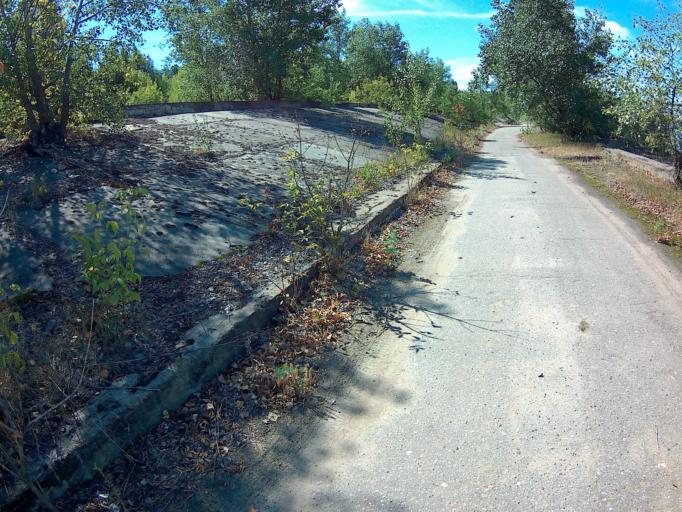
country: RU
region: Nizjnij Novgorod
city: Nizhniy Novgorod
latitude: 56.2547
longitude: 43.9609
